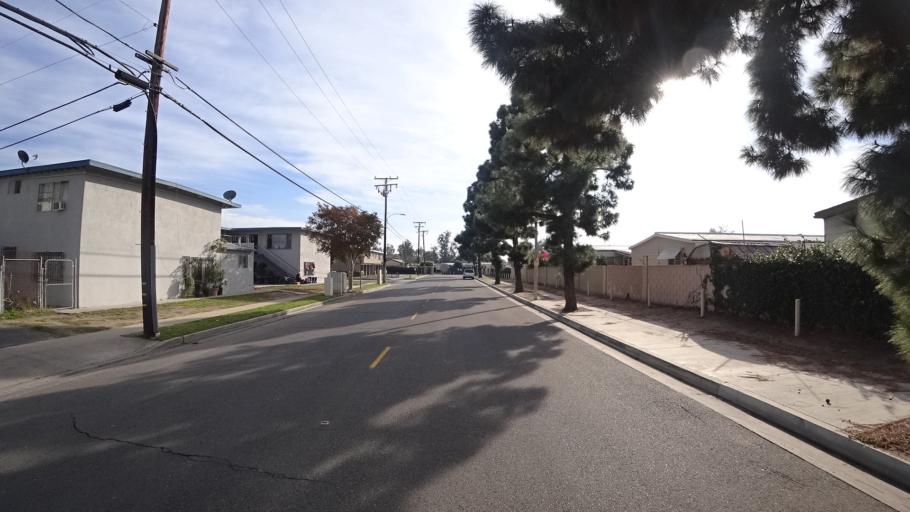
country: US
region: California
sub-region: Orange County
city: Garden Grove
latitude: 33.7572
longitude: -117.9116
